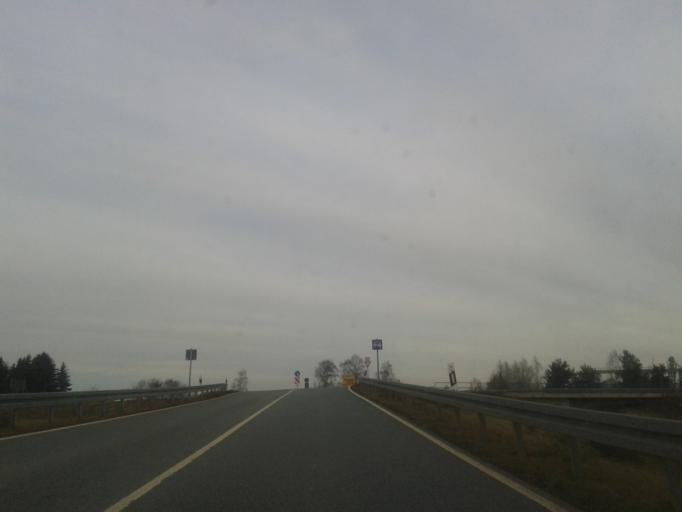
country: DE
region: Saxony
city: Herrnhut
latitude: 50.9918
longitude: 14.7147
